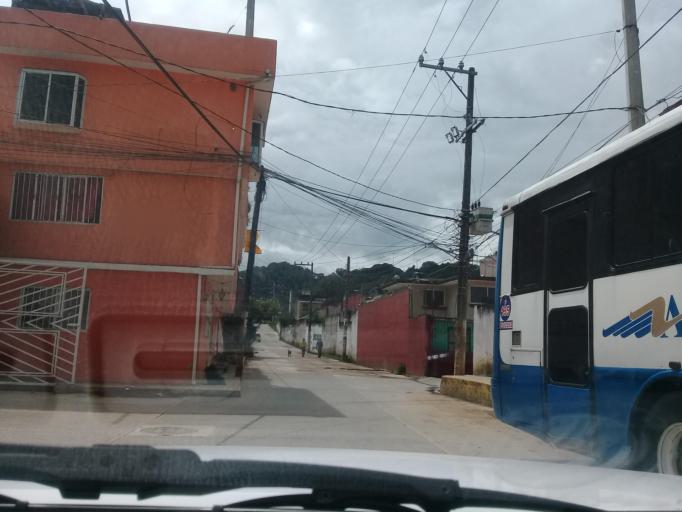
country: MX
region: Veracruz
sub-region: Rafael Lucio
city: Piletas
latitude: 19.5913
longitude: -96.9593
